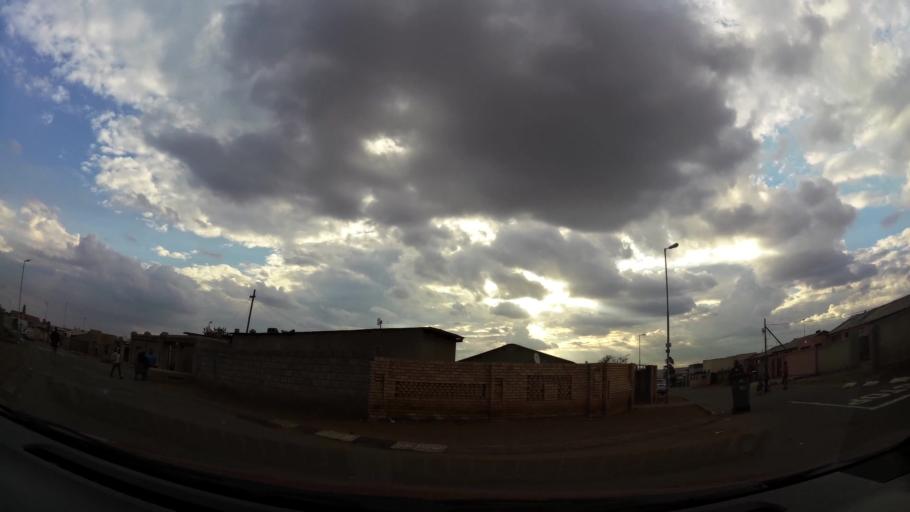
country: ZA
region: Gauteng
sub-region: City of Johannesburg Metropolitan Municipality
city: Soweto
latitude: -26.2414
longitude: 27.8223
